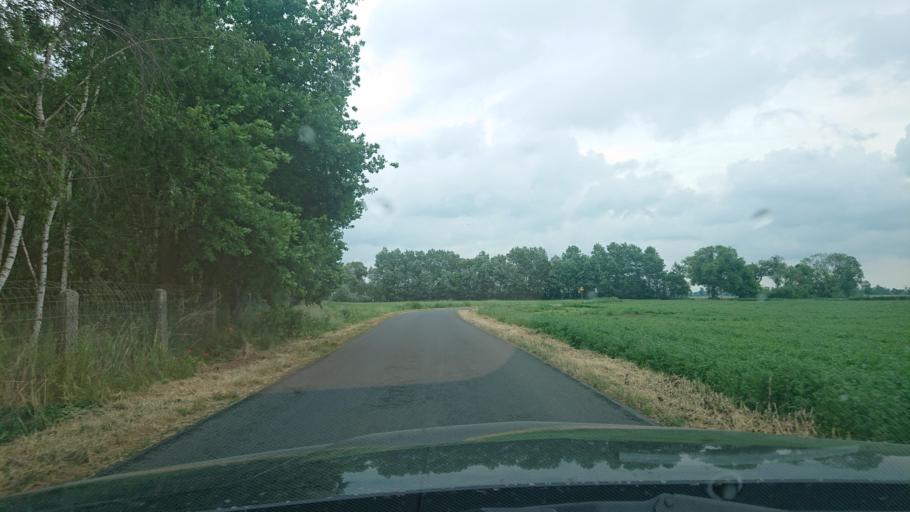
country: PL
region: Greater Poland Voivodeship
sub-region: Powiat gnieznienski
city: Czerniejewo
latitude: 52.4781
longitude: 17.5347
